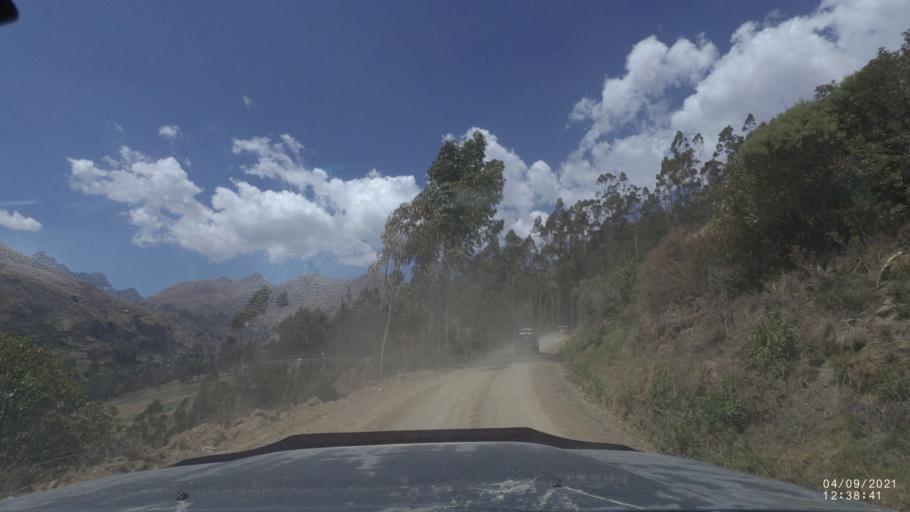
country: BO
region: Cochabamba
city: Colchani
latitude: -17.2282
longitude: -66.5009
